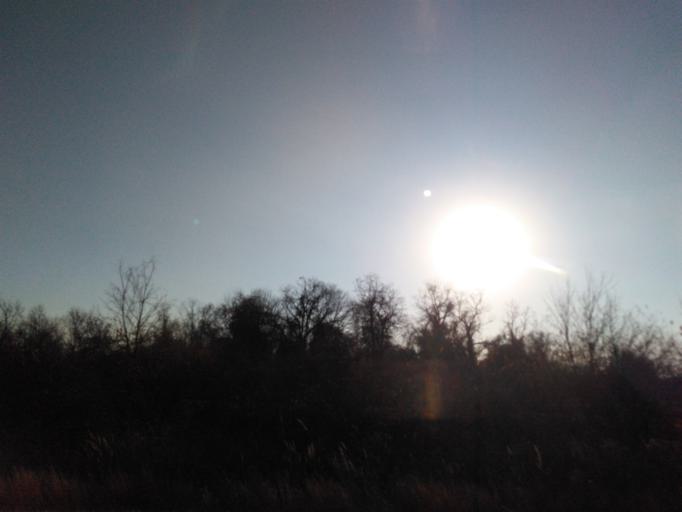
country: US
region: Illinois
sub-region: Saint Clair County
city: Alorton
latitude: 38.5941
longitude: -90.0901
